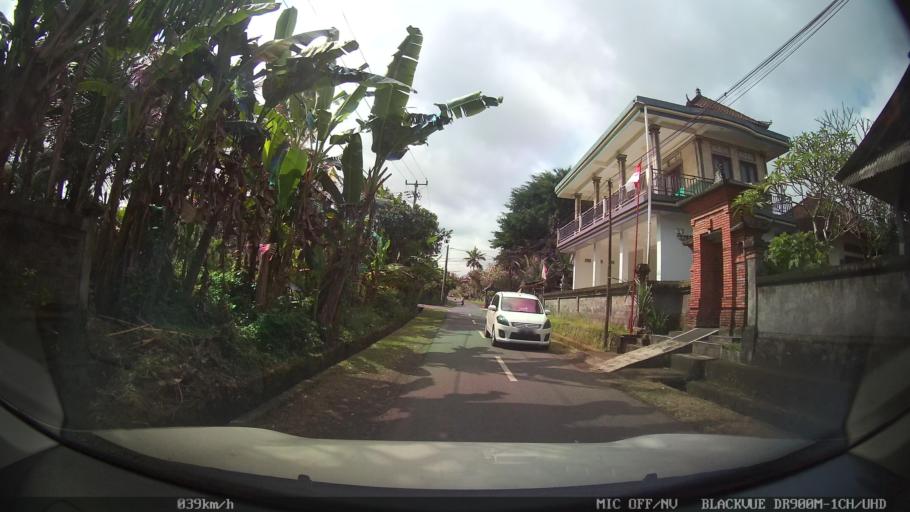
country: ID
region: Bali
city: Banjar Pesalakan
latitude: -8.5138
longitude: 115.3021
